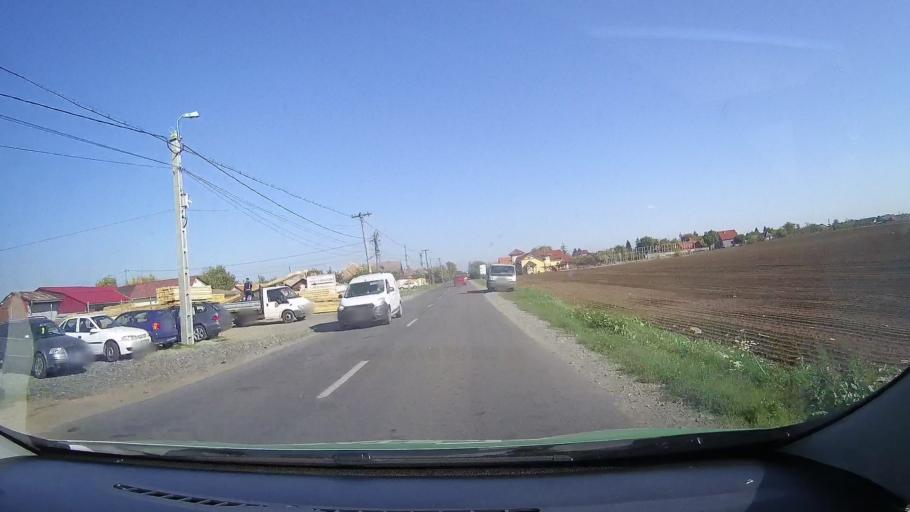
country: RO
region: Satu Mare
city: Carei
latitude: 47.6711
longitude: 22.4657
